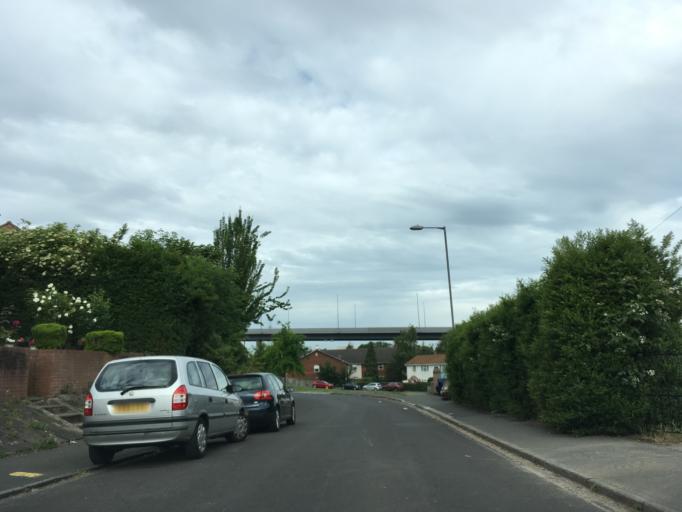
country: GB
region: England
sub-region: North Somerset
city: Easton-in-Gordano
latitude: 51.4920
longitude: -2.6851
